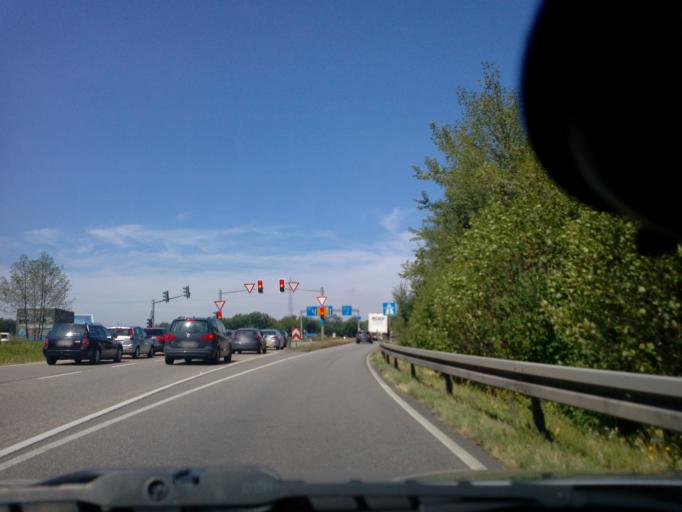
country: DE
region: Baden-Wuerttemberg
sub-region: Freiburg Region
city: Schutterwald
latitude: 48.4720
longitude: 7.9075
